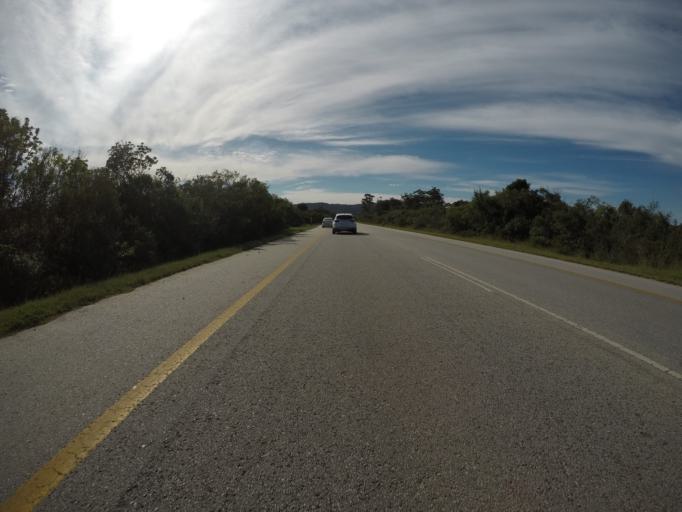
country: ZA
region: Eastern Cape
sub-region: Cacadu District Municipality
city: Jeffrey's Bay
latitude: -33.8940
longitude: 25.1294
